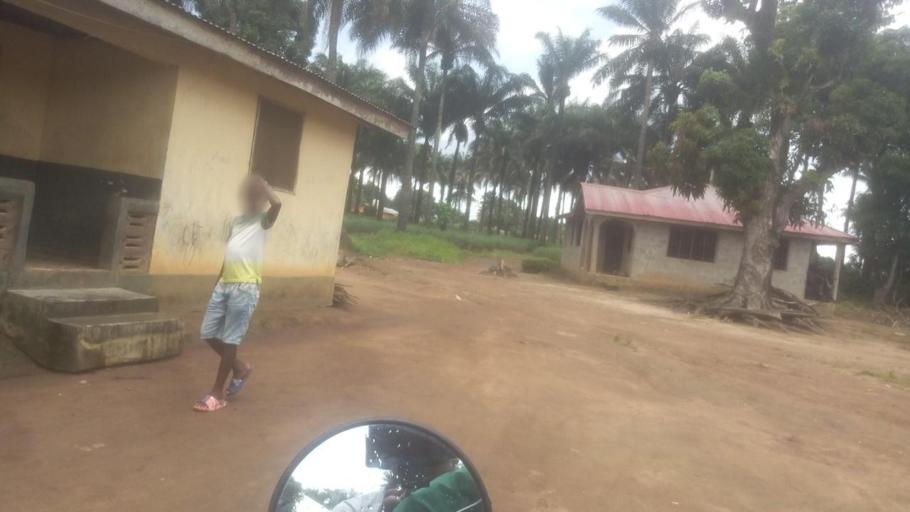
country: SL
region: Northern Province
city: Tintafor
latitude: 8.6384
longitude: -13.2189
